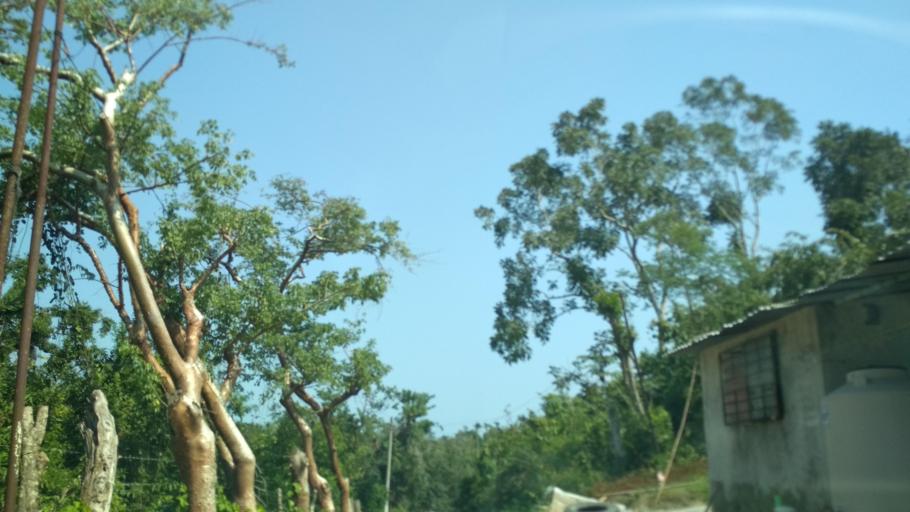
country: MX
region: Veracruz
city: Gutierrez Zamora
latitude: 20.4242
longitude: -97.1955
